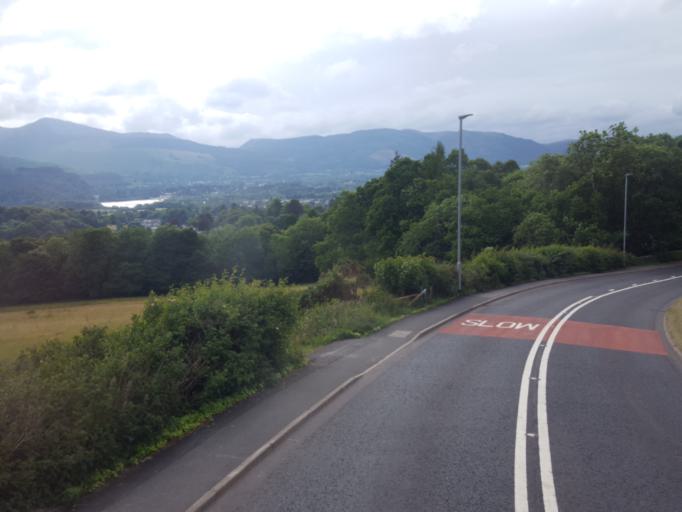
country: GB
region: England
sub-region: Cumbria
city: Keswick
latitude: 54.5966
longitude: -3.1159
